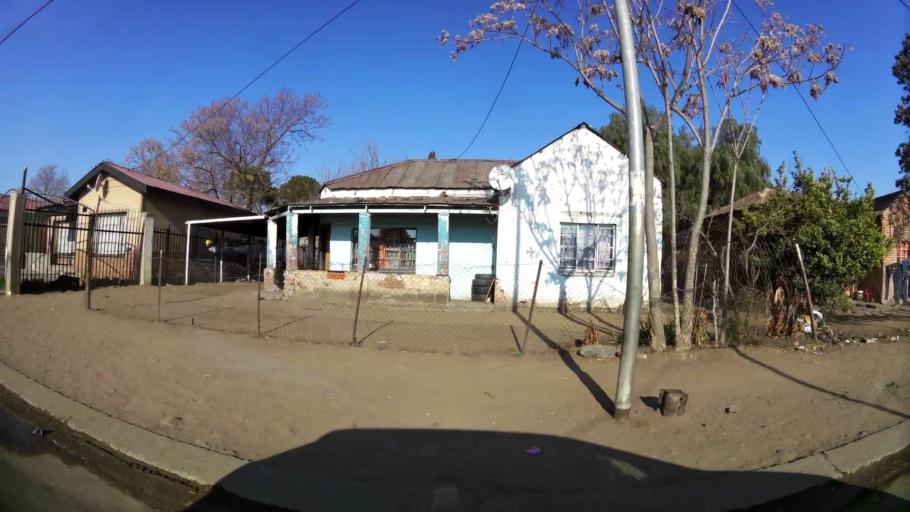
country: ZA
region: Orange Free State
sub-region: Mangaung Metropolitan Municipality
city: Bloemfontein
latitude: -29.1350
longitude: 26.2413
